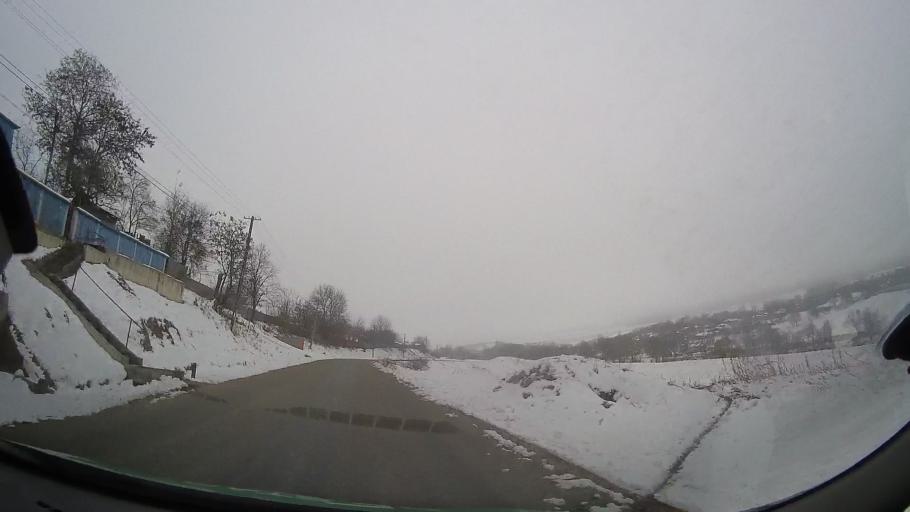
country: RO
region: Bacau
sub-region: Comuna Vultureni
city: Vultureni
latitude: 46.3317
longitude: 27.2918
